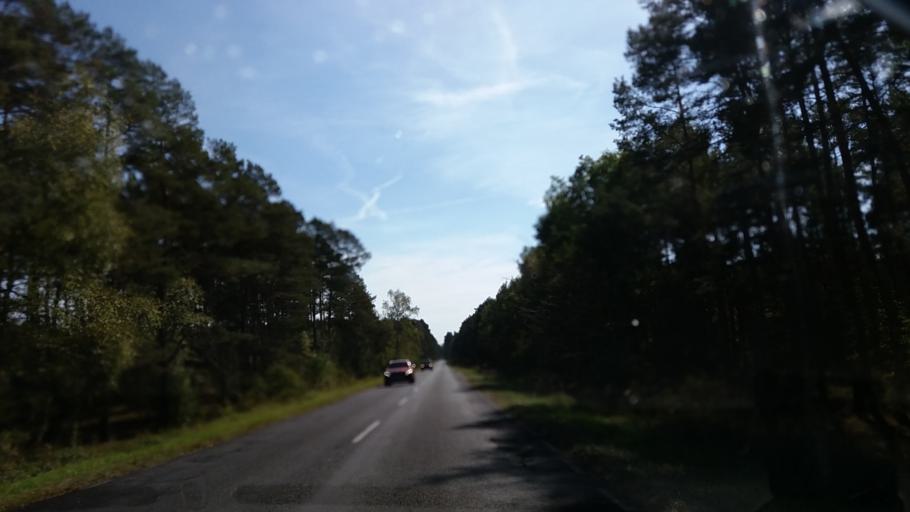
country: PL
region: Lubusz
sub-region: Powiat strzelecko-drezdenecki
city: Drezdenko
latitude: 52.7637
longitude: 15.8508
